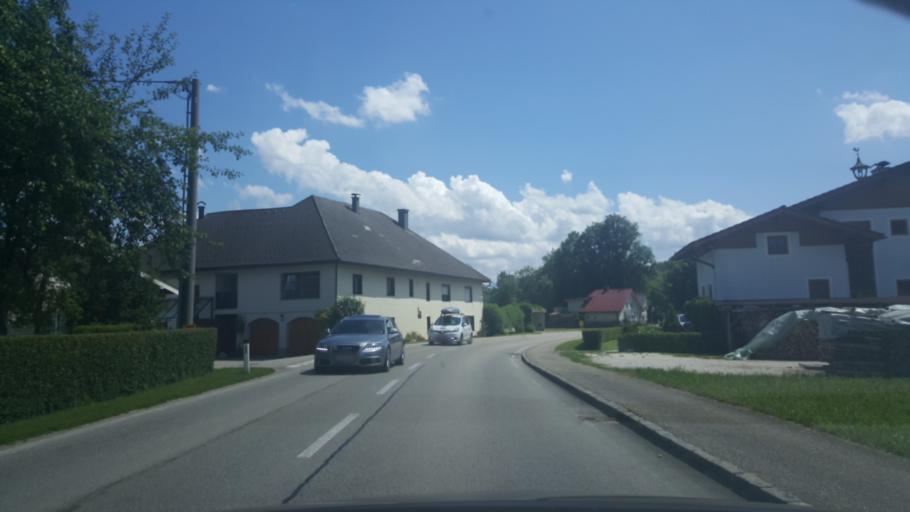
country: AT
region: Upper Austria
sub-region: Politischer Bezirk Vocklabruck
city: Gampern
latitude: 47.9971
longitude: 13.5461
